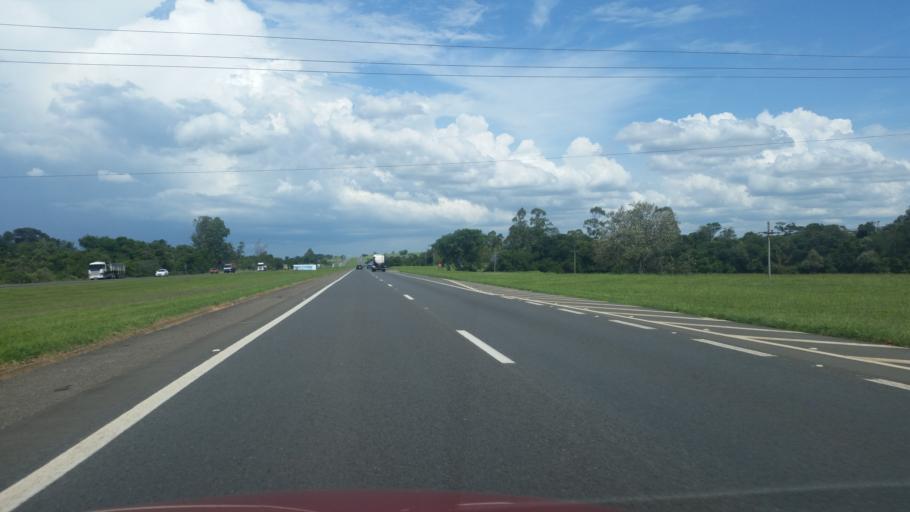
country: BR
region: Sao Paulo
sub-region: Tatui
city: Tatui
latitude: -23.2543
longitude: -47.9327
